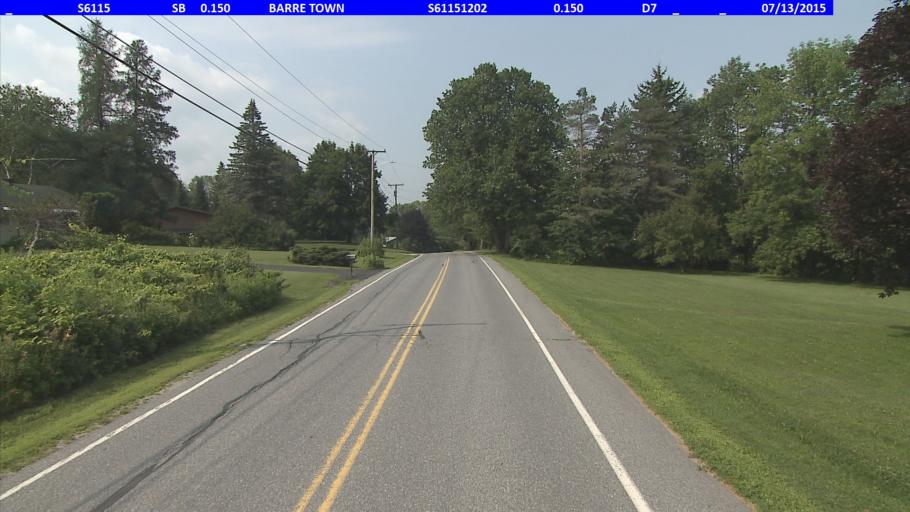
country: US
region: Vermont
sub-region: Washington County
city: Barre
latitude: 44.2026
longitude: -72.4862
